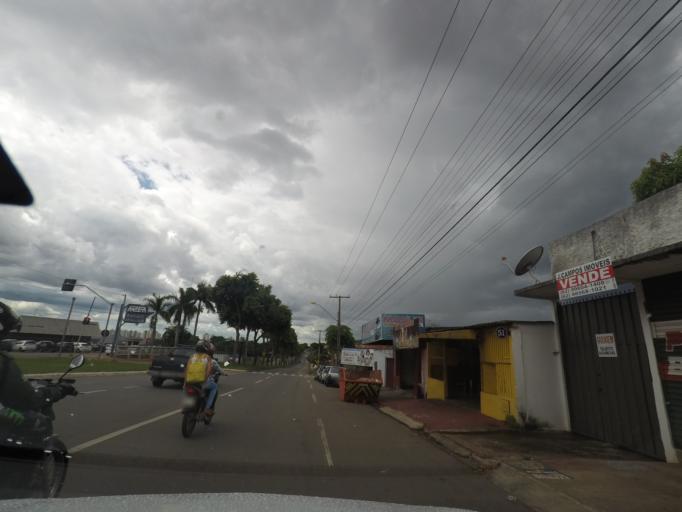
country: BR
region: Goias
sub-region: Goiania
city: Goiania
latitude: -16.7321
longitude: -49.3253
